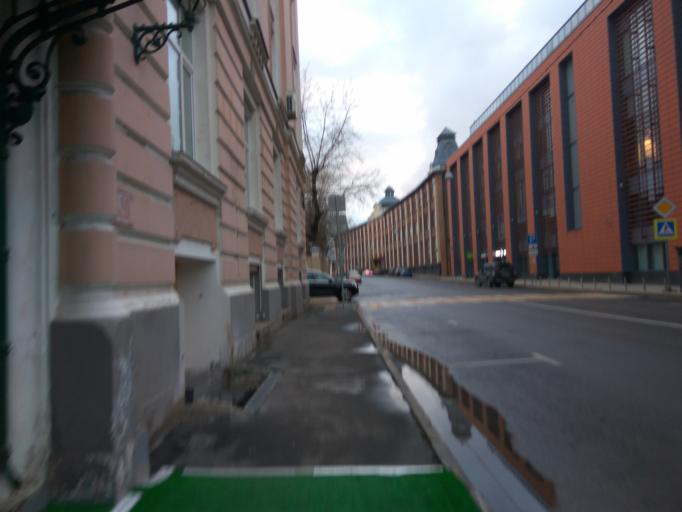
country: RU
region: Moscow
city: Taganskiy
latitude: 55.7459
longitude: 37.6646
